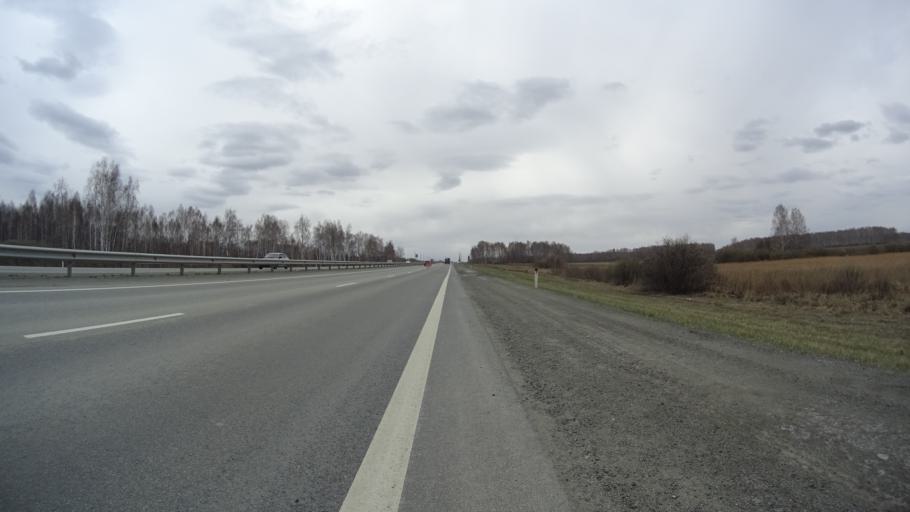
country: RU
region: Chelyabinsk
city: Yemanzhelinka
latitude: 54.8389
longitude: 61.3132
